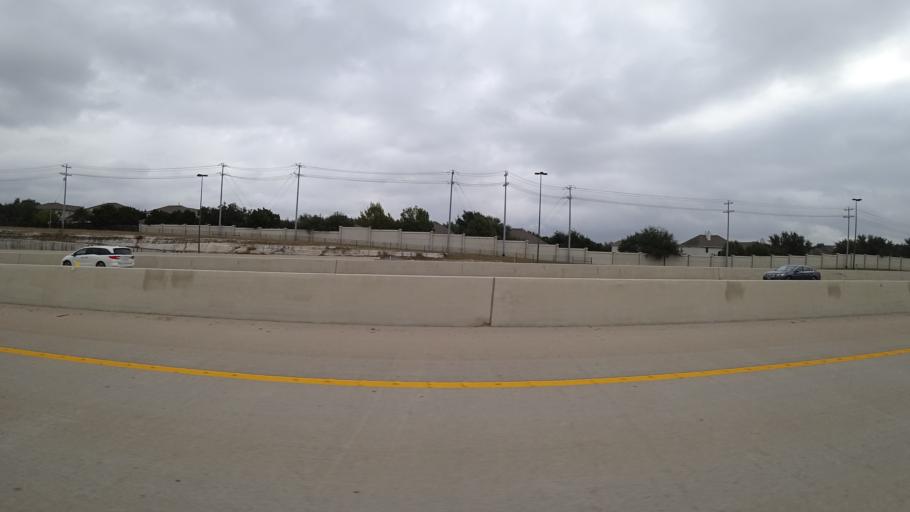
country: US
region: Texas
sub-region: Williamson County
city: Cedar Park
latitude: 30.5124
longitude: -97.8126
